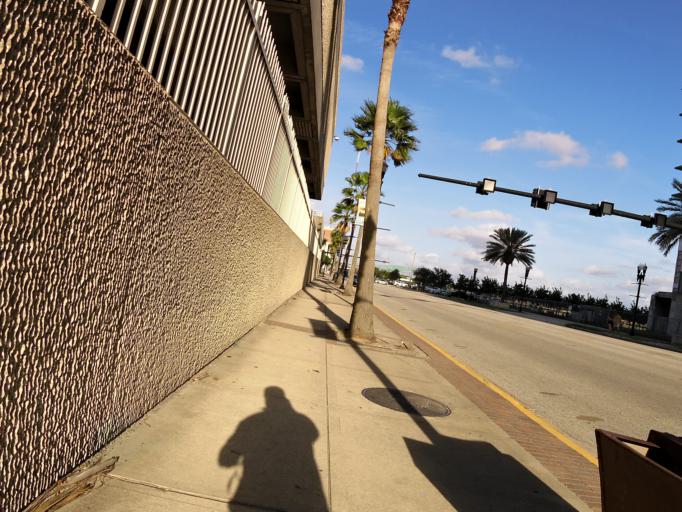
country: US
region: Florida
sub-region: Duval County
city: Jacksonville
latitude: 30.3246
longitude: -81.6515
